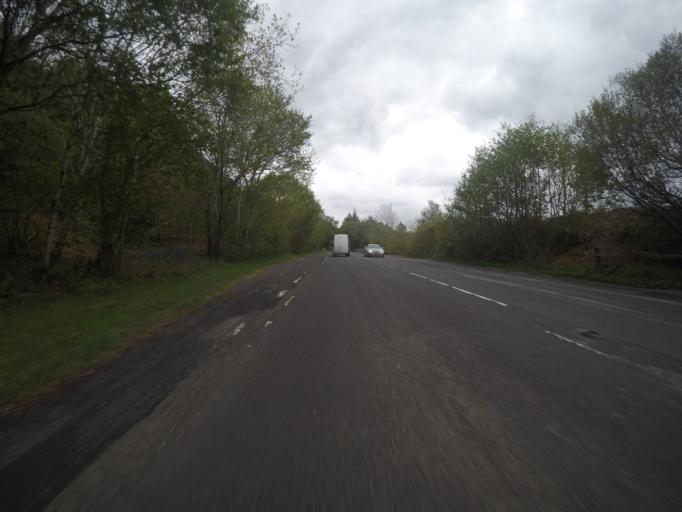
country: GB
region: Scotland
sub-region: Highland
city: Fort William
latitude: 57.2509
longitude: -5.4732
